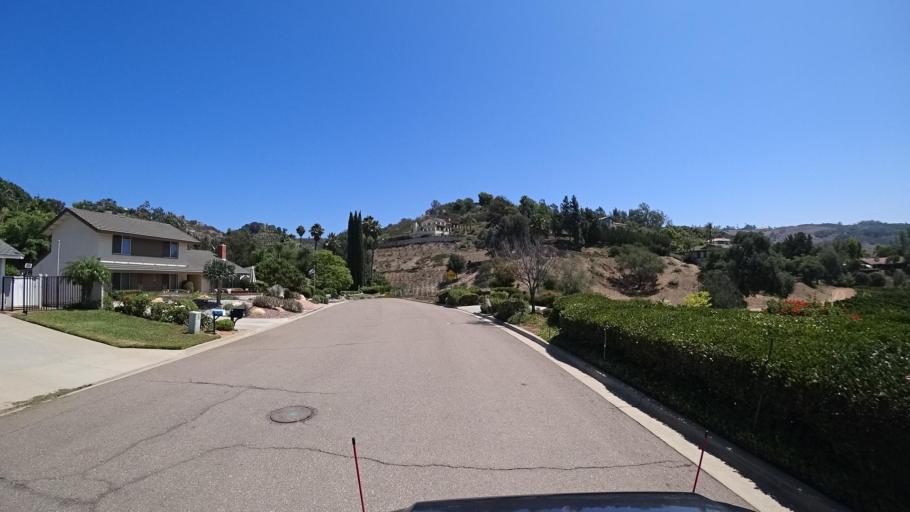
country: US
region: California
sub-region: San Diego County
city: Bonsall
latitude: 33.3420
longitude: -117.1856
